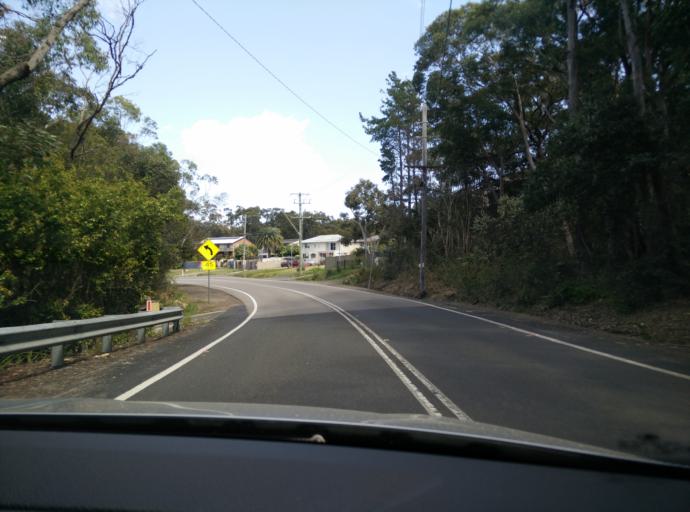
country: AU
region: New South Wales
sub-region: Gosford Shire
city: Blackwall
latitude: -33.4920
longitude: 151.2996
